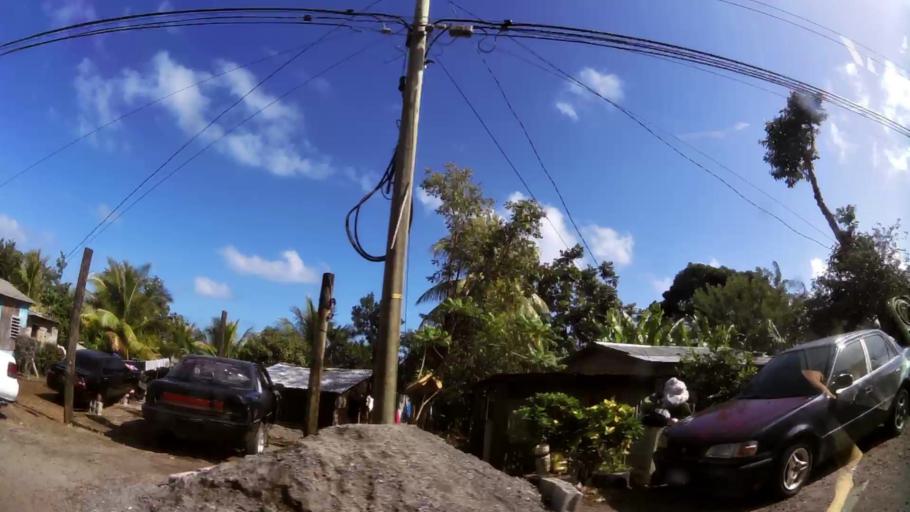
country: DM
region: Saint David
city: Castle Bruce
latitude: 15.4837
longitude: -61.2522
